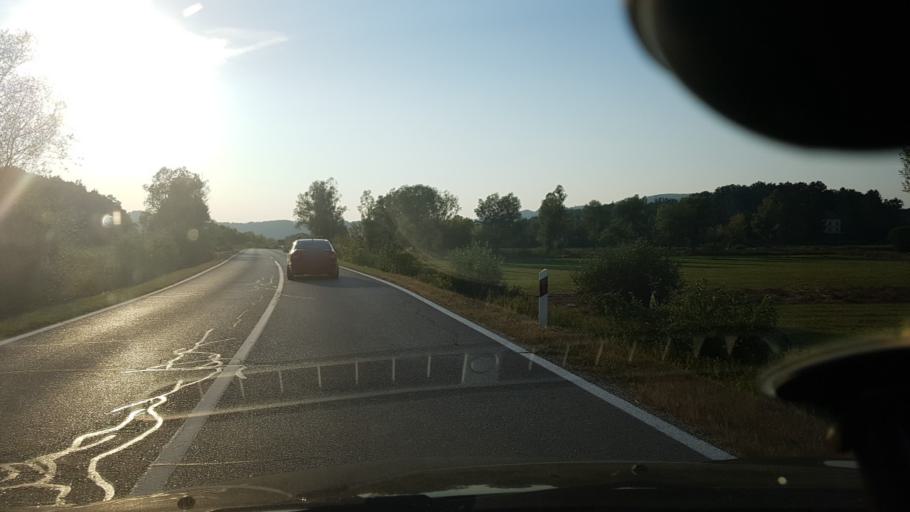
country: HR
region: Krapinsko-Zagorska
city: Pregrada
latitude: 46.1412
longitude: 15.7876
